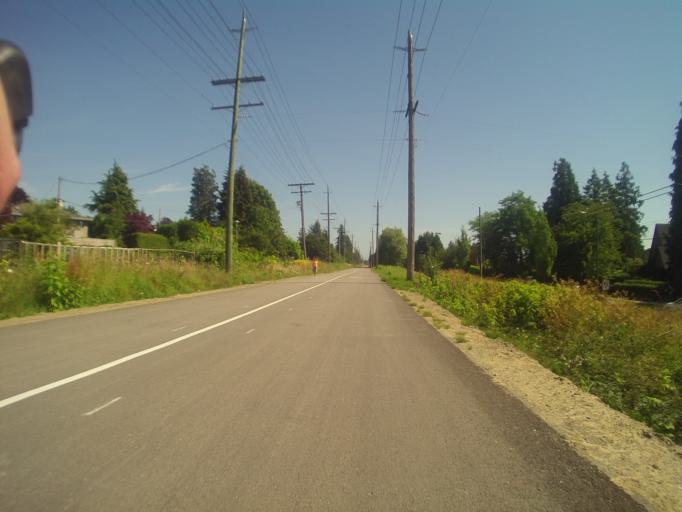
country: CA
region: British Columbia
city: Vancouver
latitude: 49.2232
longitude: -123.1525
